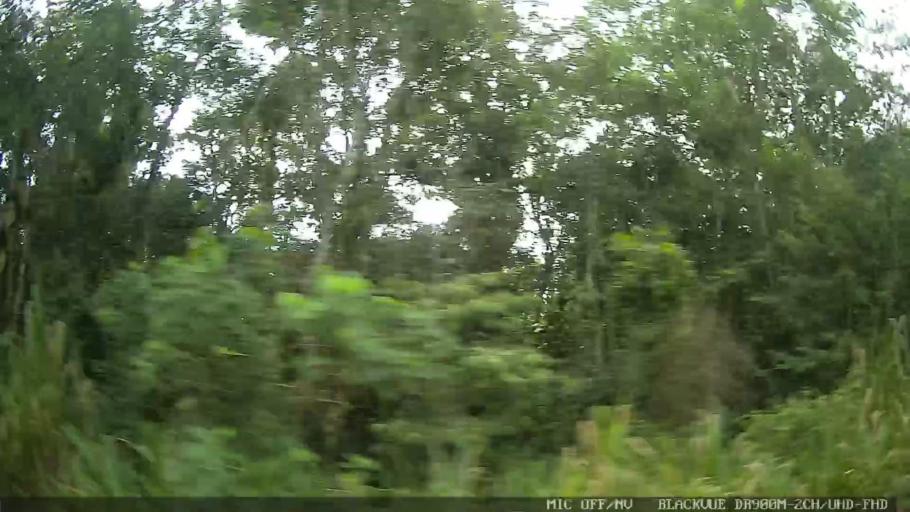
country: BR
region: Sao Paulo
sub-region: Itanhaem
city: Itanhaem
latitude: -24.1115
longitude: -46.7978
